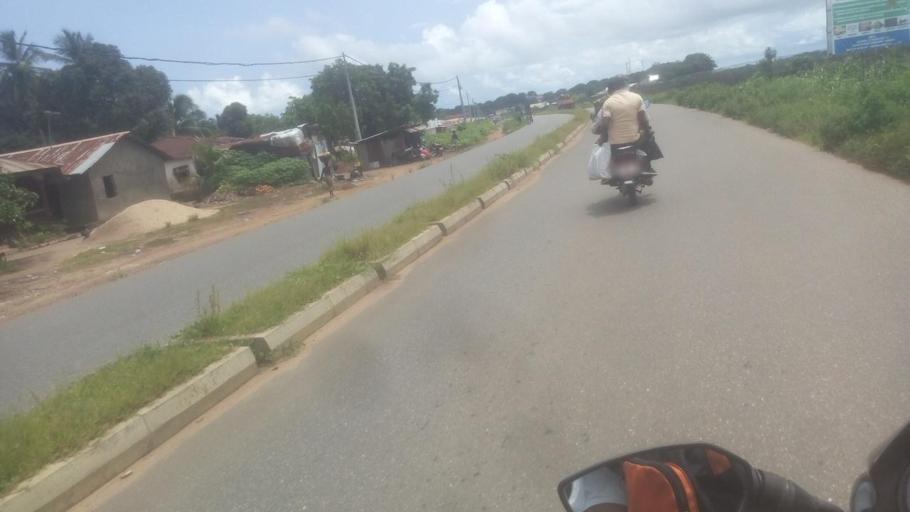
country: SL
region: Northern Province
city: Masoyila
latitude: 8.6125
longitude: -13.1905
